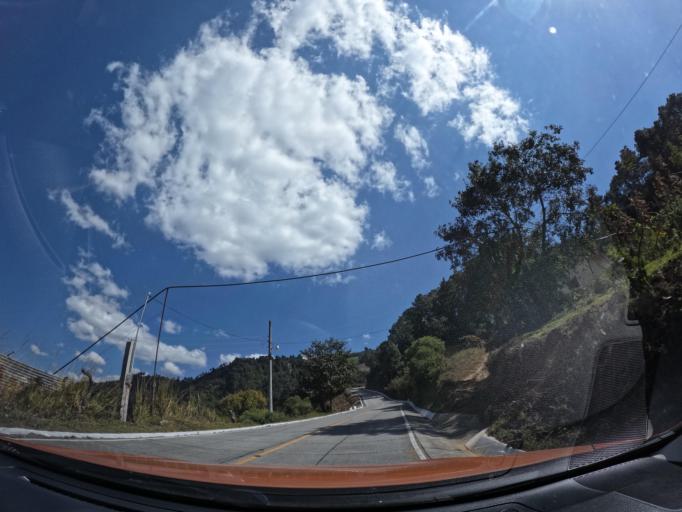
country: GT
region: Solola
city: San Antonio Palopo
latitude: 14.6914
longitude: -91.0751
